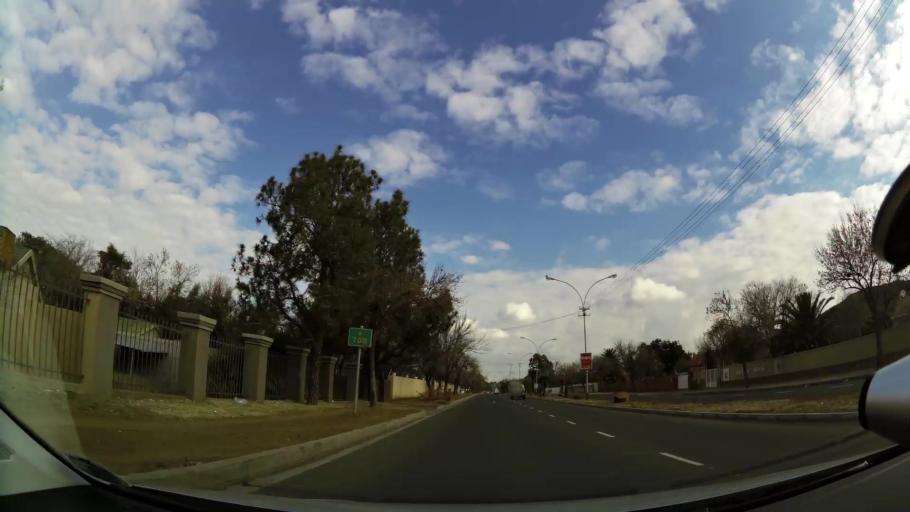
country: ZA
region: Orange Free State
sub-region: Mangaung Metropolitan Municipality
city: Bloemfontein
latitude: -29.0804
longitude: 26.2352
